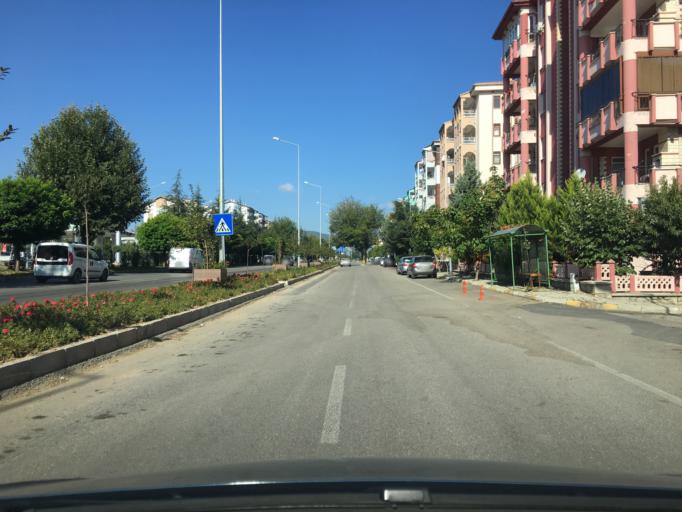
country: TR
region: Isparta
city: Isparta
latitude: 37.7897
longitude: 30.5505
